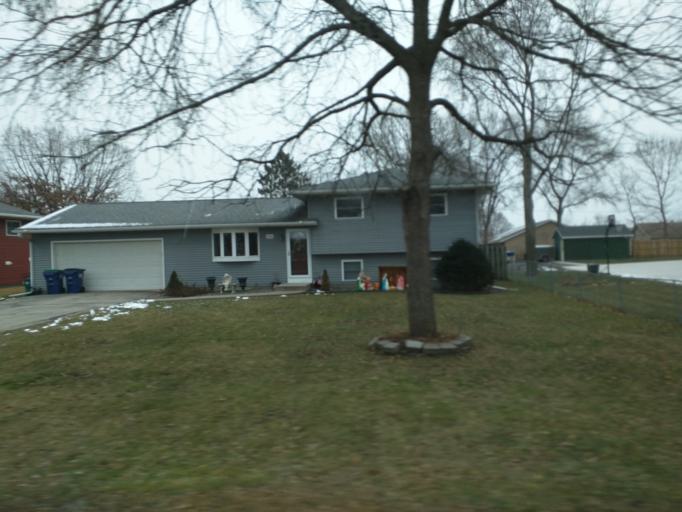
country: US
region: Wisconsin
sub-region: La Crosse County
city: French Island
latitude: 43.8615
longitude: -91.2698
